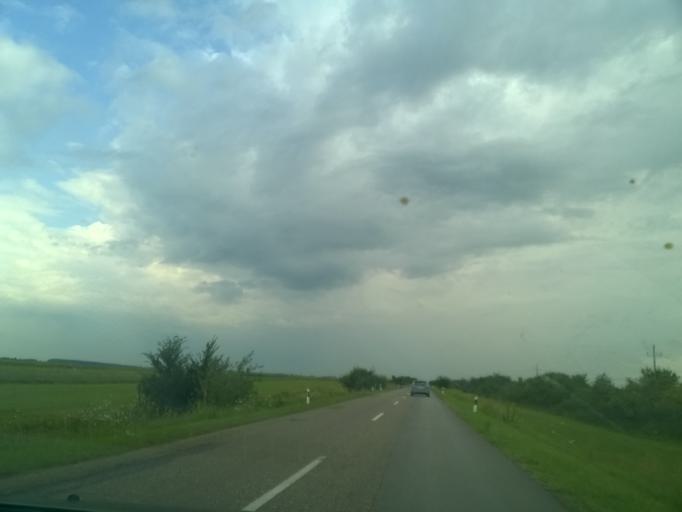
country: RS
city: Uzdin
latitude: 45.2327
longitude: 20.6265
